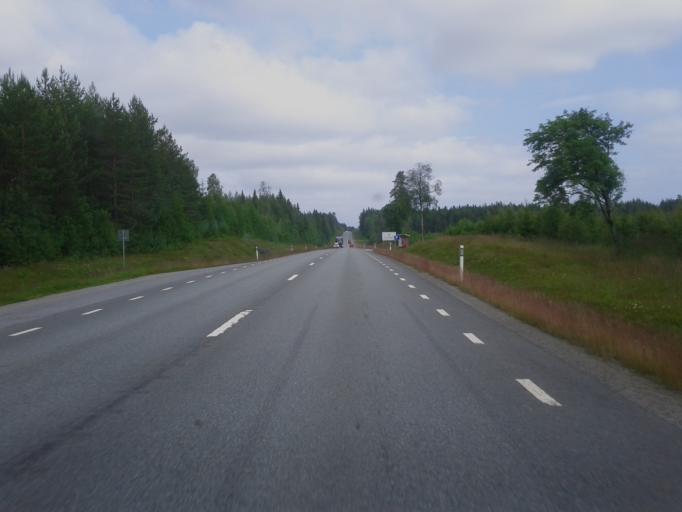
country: SE
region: Vaesterbotten
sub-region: Skelleftea Kommun
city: Burea
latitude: 64.3527
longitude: 21.2938
